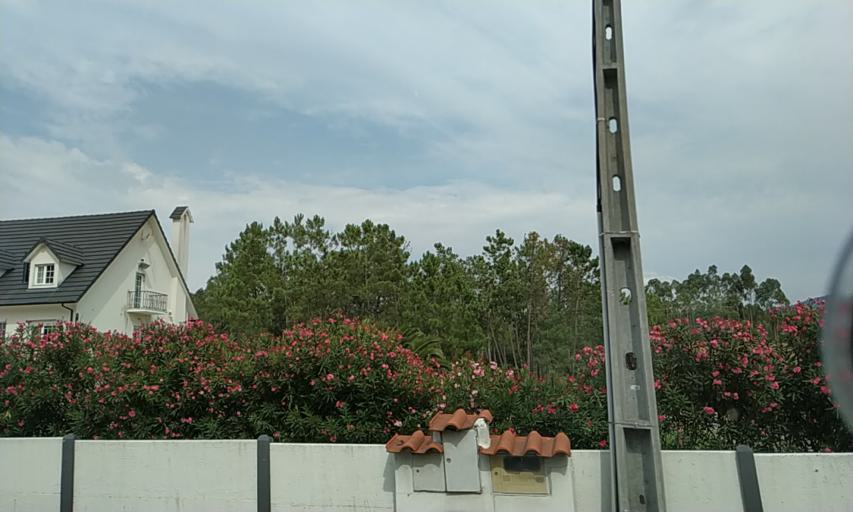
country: PT
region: Coimbra
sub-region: Soure
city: Soure
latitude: 40.0410
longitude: -8.5567
